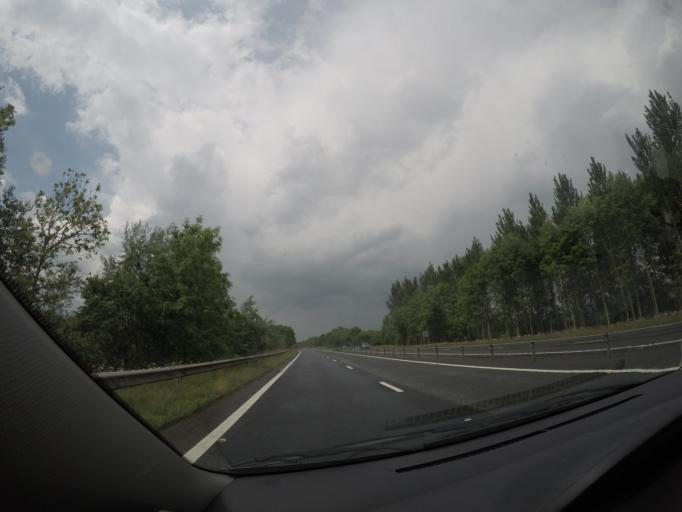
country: GB
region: England
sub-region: Cumbria
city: Appleby-in-Westmorland
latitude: 54.5761
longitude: -2.4690
